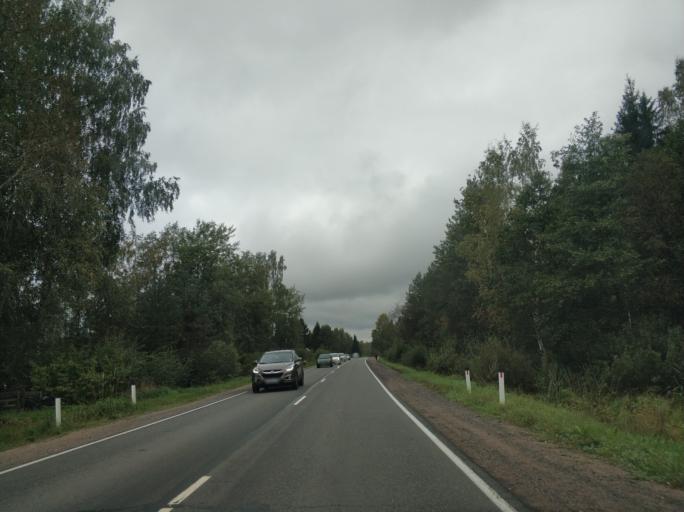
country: RU
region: Leningrad
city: Shcheglovo
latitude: 60.0934
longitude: 30.8520
